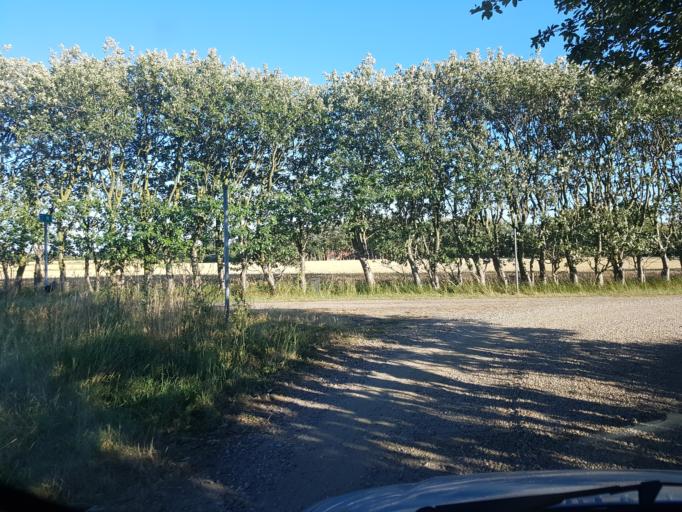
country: DK
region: South Denmark
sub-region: Esbjerg Kommune
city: Esbjerg
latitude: 55.4931
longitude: 8.5050
